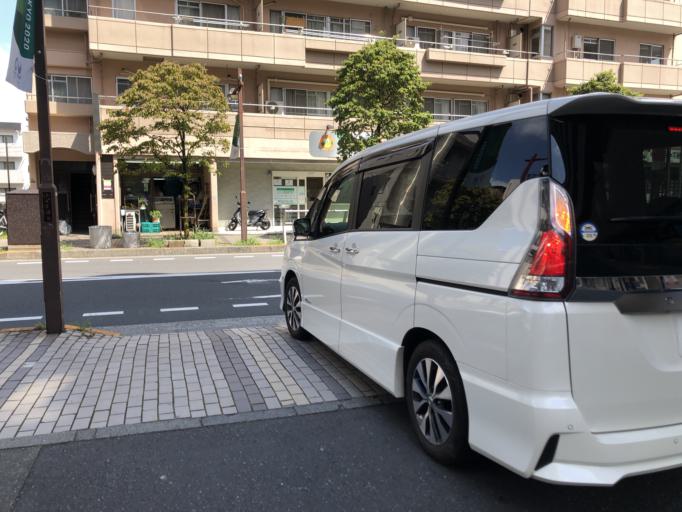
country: JP
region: Tokyo
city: Kamirenjaku
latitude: 35.7041
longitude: 139.5449
